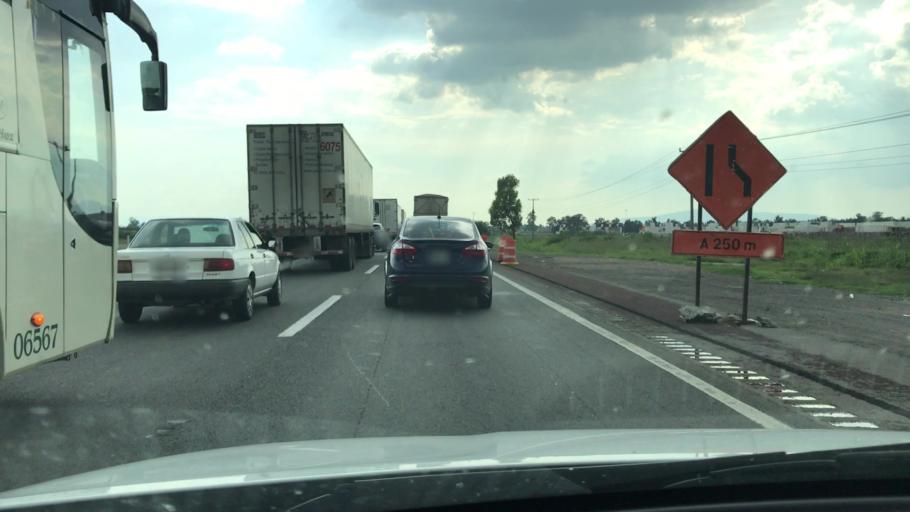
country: MX
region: Guanajuato
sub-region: Irapuato
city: Cuarta Brigada
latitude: 20.6536
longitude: -101.3057
